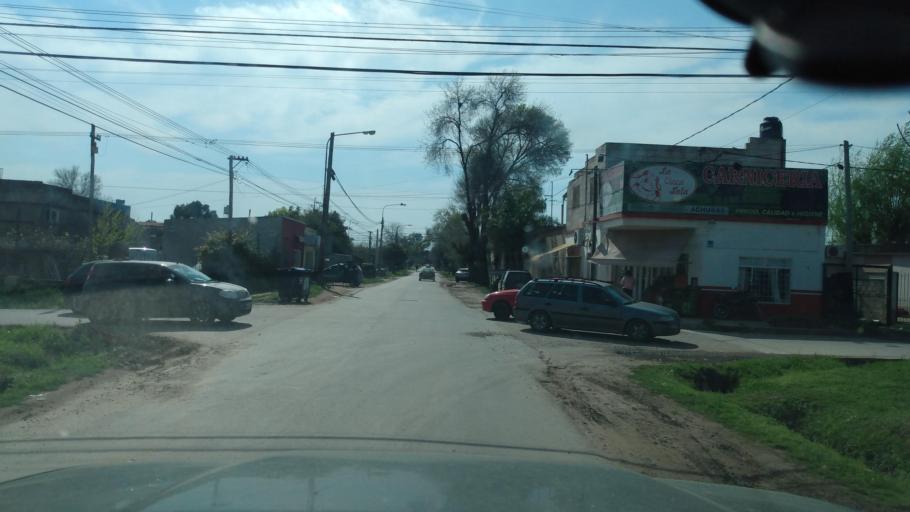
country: AR
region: Buenos Aires
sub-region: Partido de Lujan
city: Lujan
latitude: -34.5513
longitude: -59.1063
